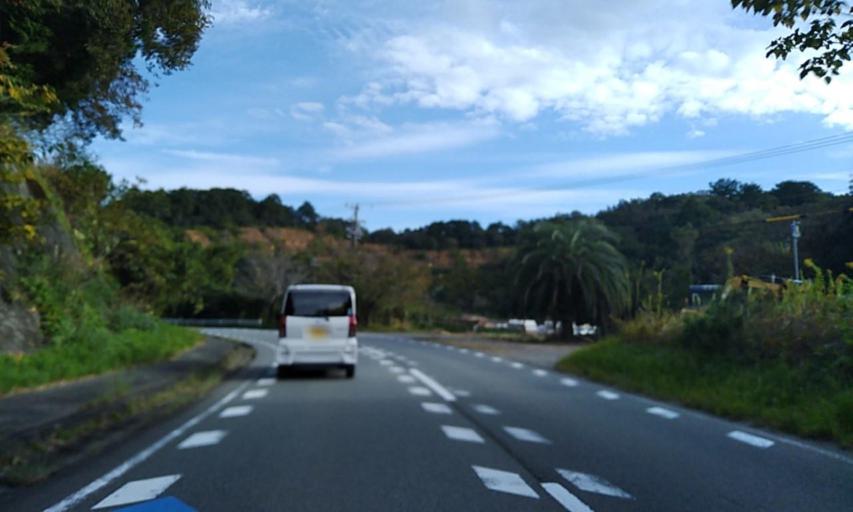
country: JP
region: Mie
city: Ise
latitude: 34.3456
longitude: 136.7151
